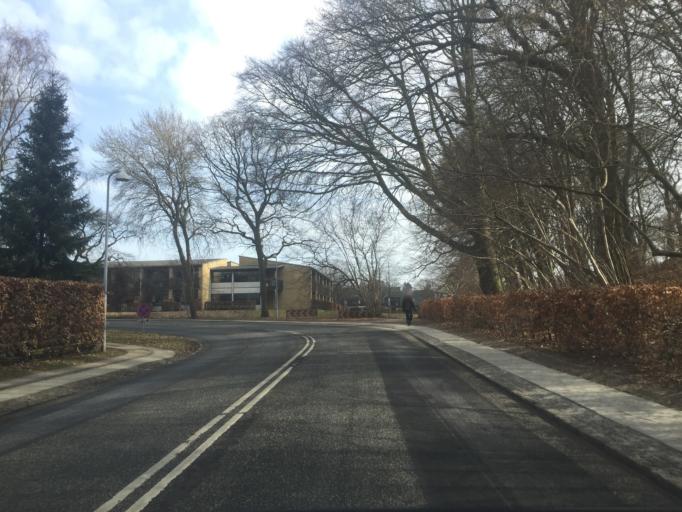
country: DK
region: Capital Region
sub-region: Lyngby-Tarbaek Kommune
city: Kongens Lyngby
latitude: 55.7908
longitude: 12.5038
